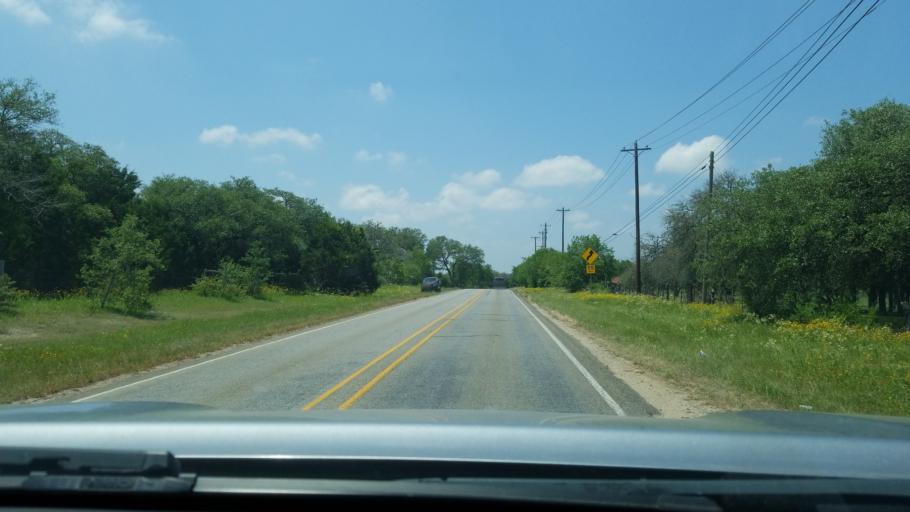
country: US
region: Texas
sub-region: Hays County
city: Woodcreek
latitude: 30.0333
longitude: -98.1752
